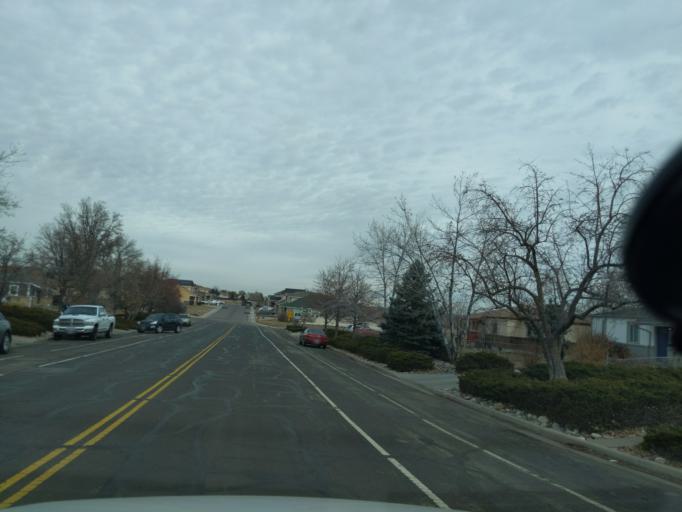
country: US
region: Colorado
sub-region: Adams County
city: Thornton
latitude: 39.8644
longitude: -104.9503
